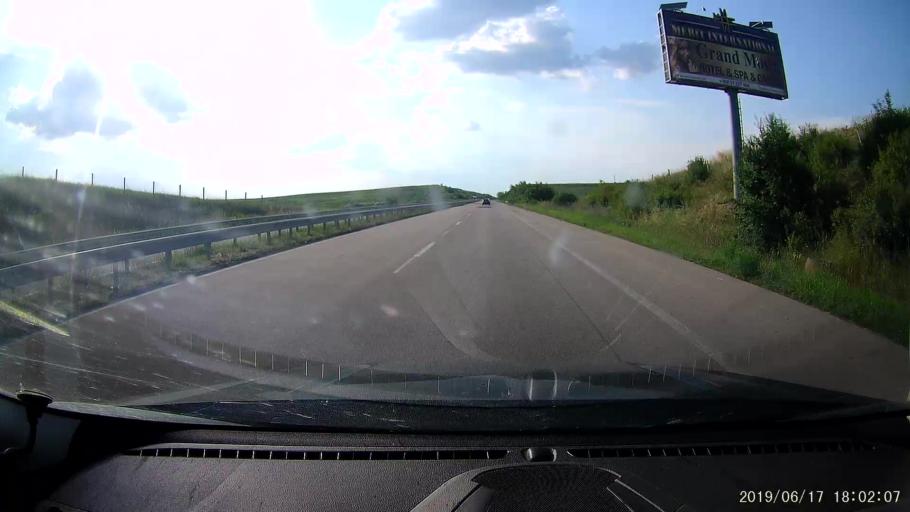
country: BG
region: Khaskovo
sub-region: Obshtina Svilengrad
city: Svilengrad
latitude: 41.7540
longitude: 26.2372
